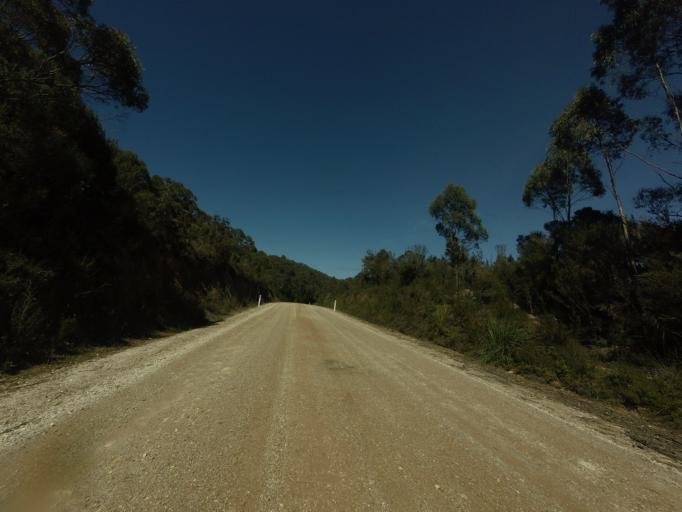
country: AU
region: Tasmania
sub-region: Huon Valley
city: Geeveston
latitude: -42.9942
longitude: 146.3711
